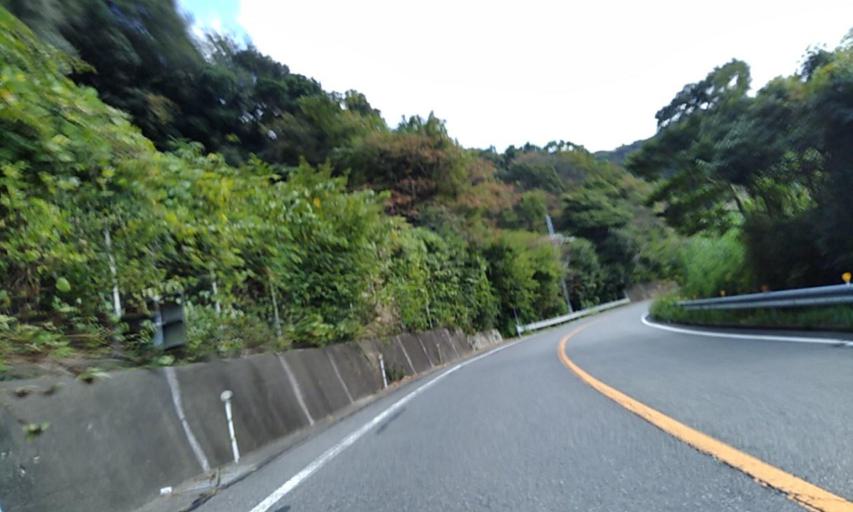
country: JP
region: Wakayama
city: Gobo
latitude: 33.9539
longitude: 135.1247
